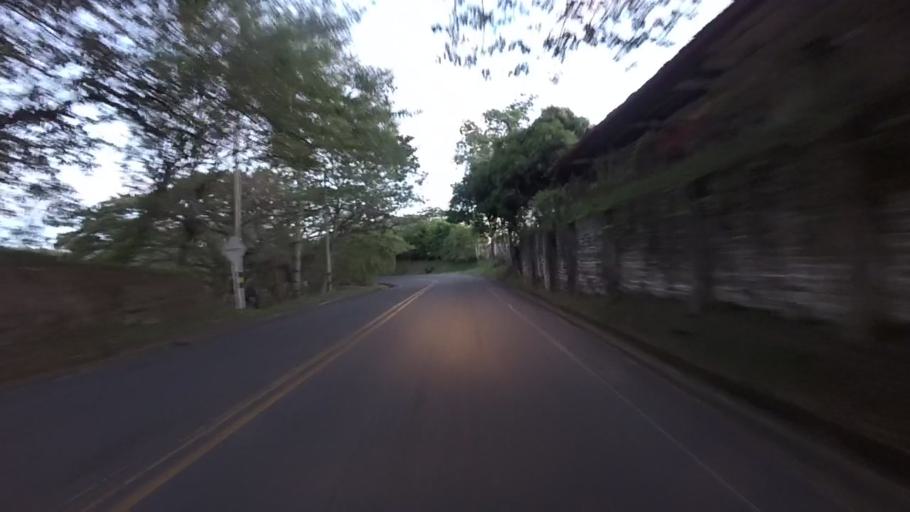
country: CO
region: Valle del Cauca
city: Cartago
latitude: 4.7264
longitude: -75.8904
